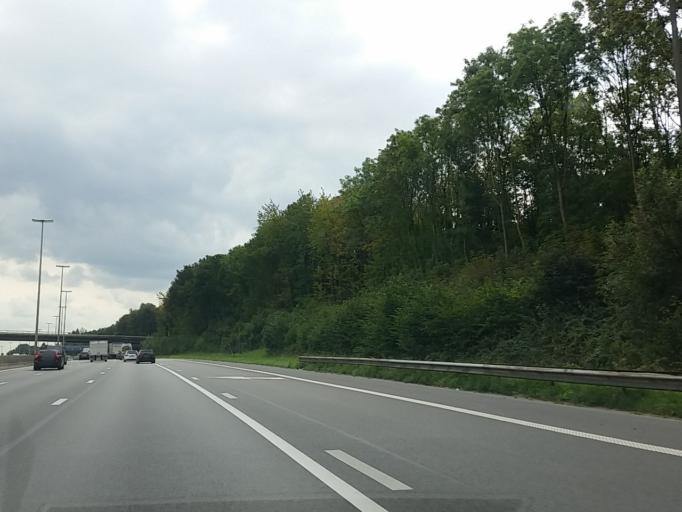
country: BE
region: Flanders
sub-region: Provincie Vlaams-Brabant
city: Dilbeek
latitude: 50.8526
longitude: 4.2745
